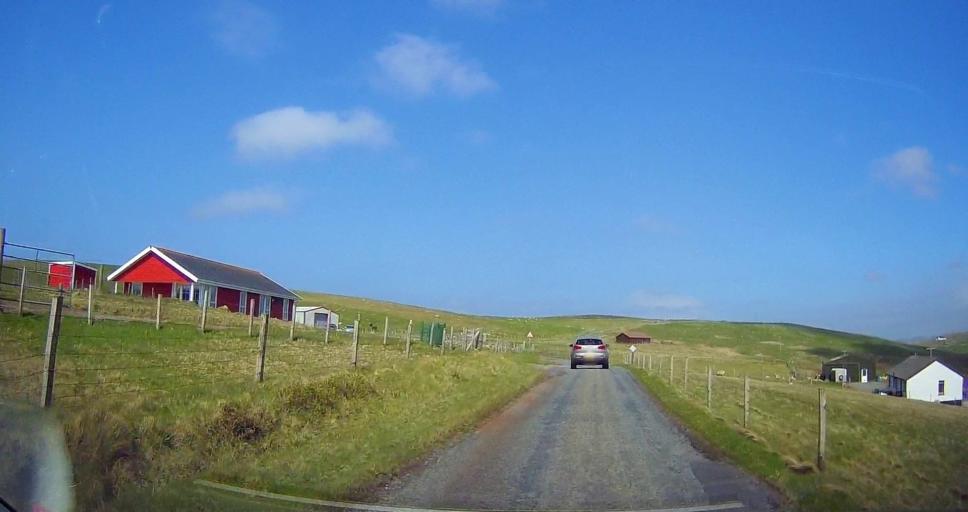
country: GB
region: Scotland
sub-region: Shetland Islands
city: Sandwick
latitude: 60.0694
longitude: -1.3398
